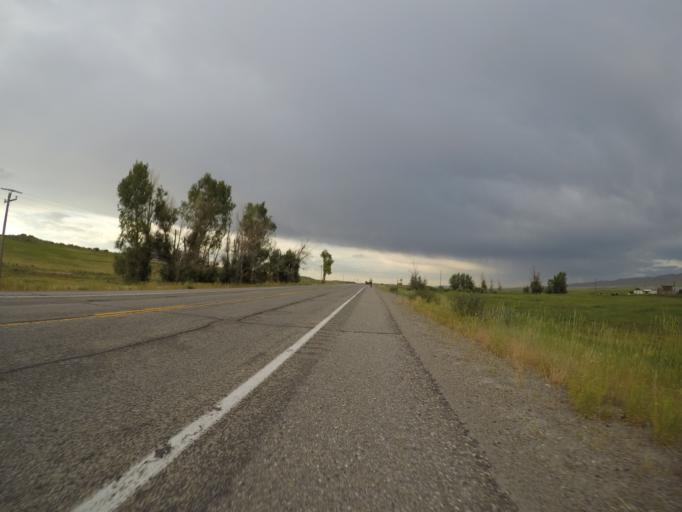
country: US
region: Idaho
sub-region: Bear Lake County
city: Montpelier
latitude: 42.0498
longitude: -110.9314
